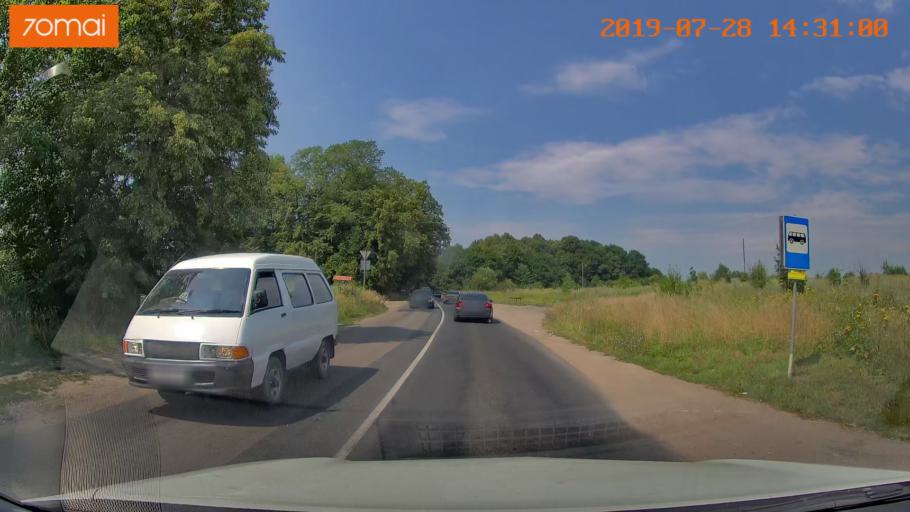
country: RU
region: Kaliningrad
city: Primorsk
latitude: 54.8039
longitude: 20.0546
